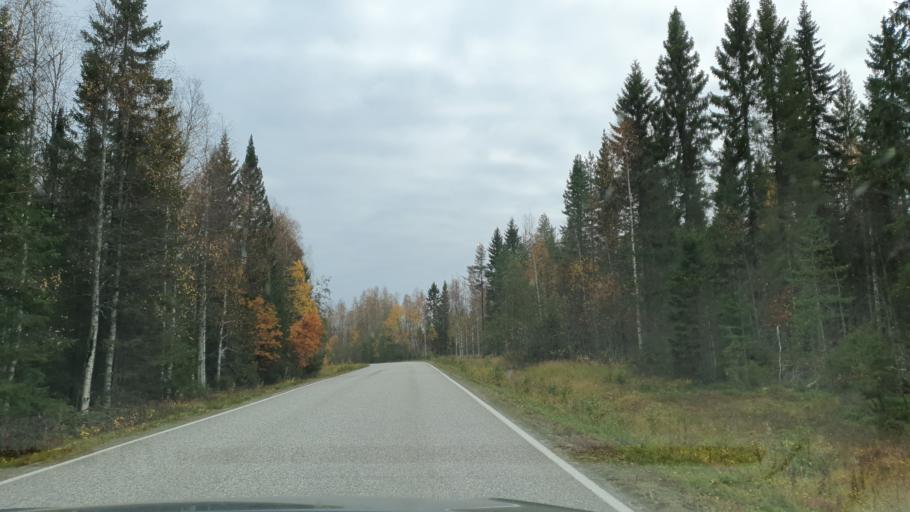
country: FI
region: Kainuu
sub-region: Kajaani
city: Ristijaervi
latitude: 64.4764
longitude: 28.2830
